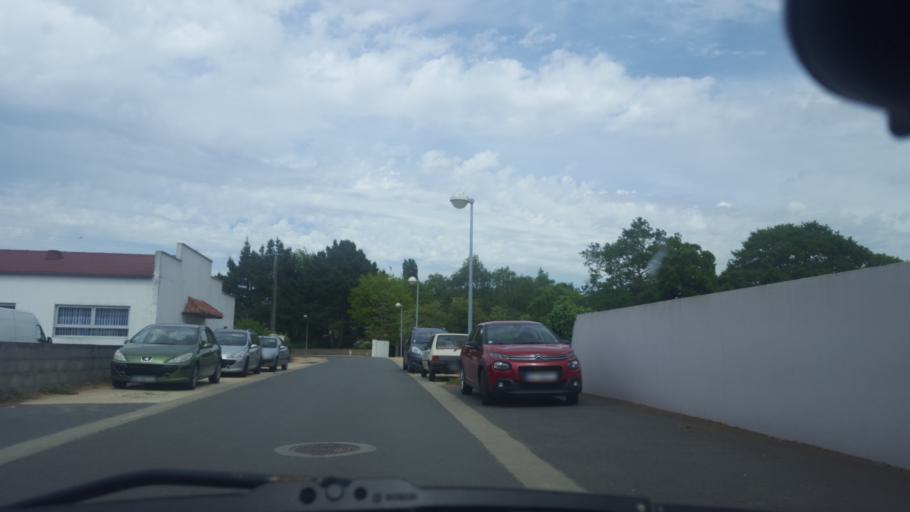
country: FR
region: Pays de la Loire
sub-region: Departement de la Loire-Atlantique
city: Paulx
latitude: 46.9619
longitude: -1.7573
